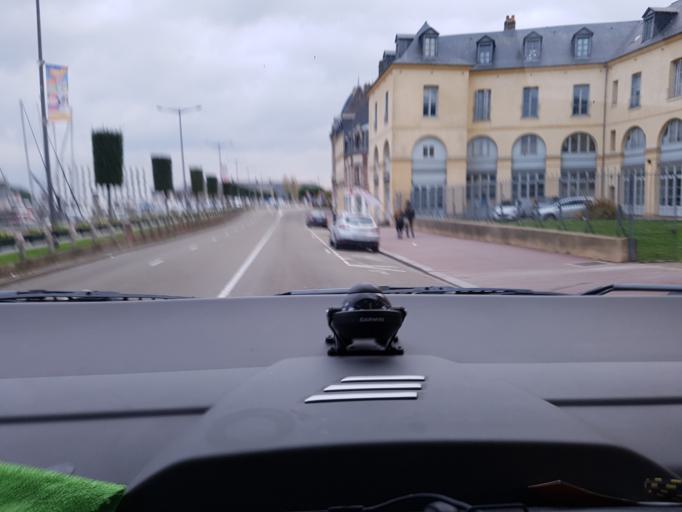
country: FR
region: Haute-Normandie
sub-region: Departement de la Seine-Maritime
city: Dieppe
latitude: 49.9247
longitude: 1.0805
